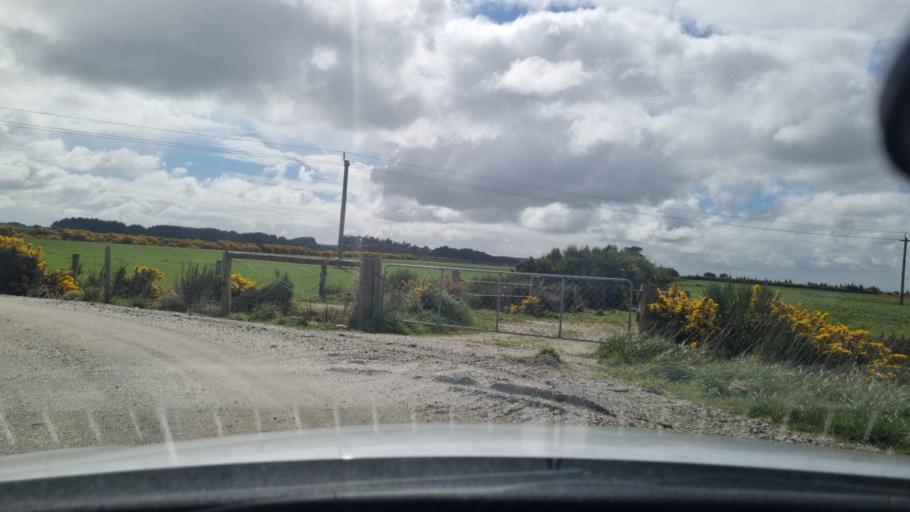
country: NZ
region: Southland
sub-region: Invercargill City
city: Bluff
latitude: -46.5259
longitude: 168.3078
